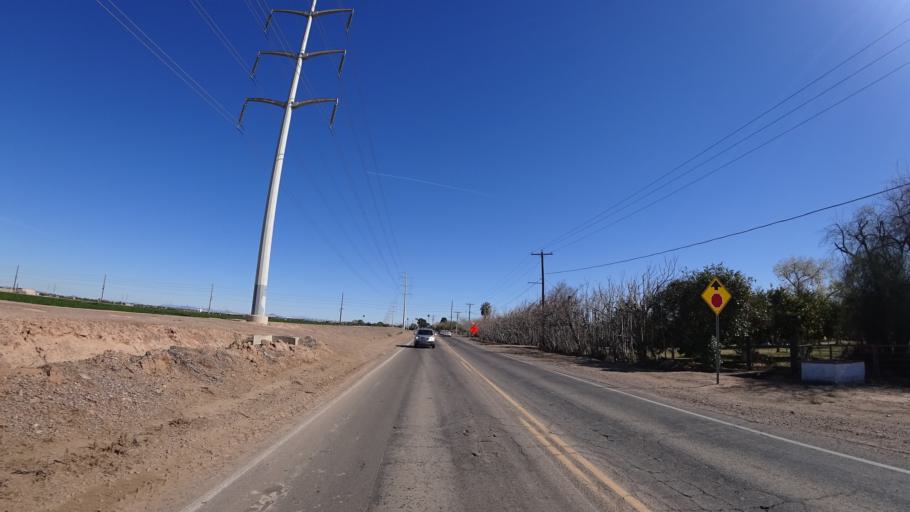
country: US
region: Arizona
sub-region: Maricopa County
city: Tolleson
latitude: 33.4065
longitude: -112.2572
